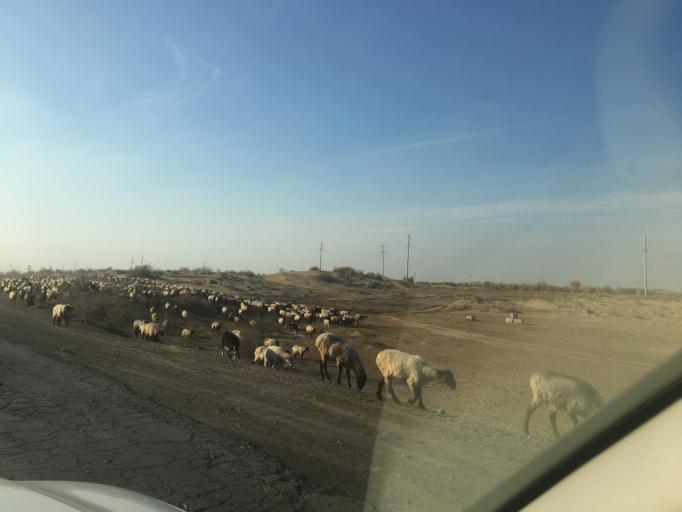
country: TM
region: Mary
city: Mary
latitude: 37.4528
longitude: 61.1958
